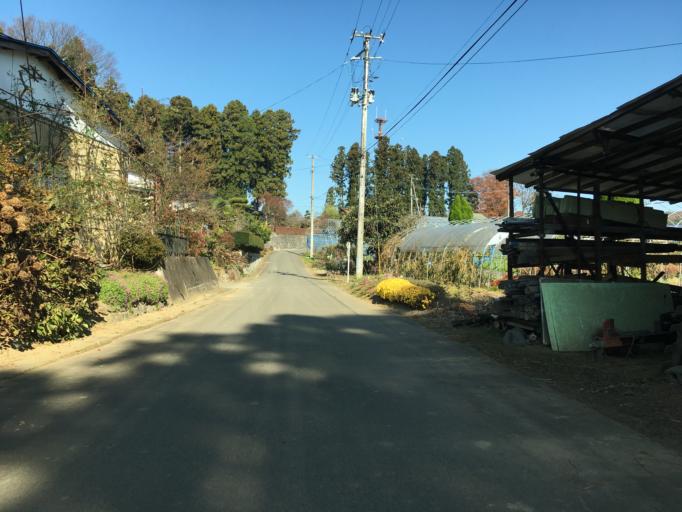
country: JP
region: Fukushima
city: Nihommatsu
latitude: 37.5798
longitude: 140.3903
